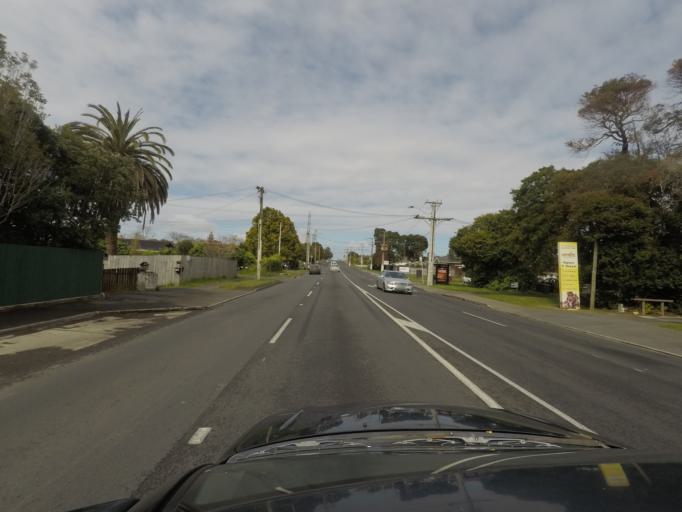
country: NZ
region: Auckland
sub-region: Auckland
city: Tamaki
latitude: -36.9047
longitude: 174.8411
